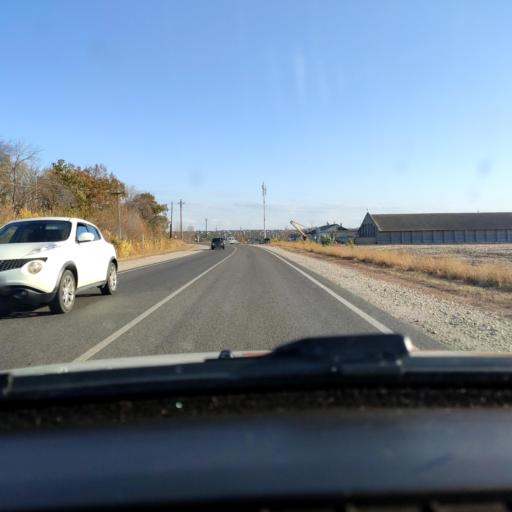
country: RU
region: Voronezj
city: Semiluki
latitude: 51.7244
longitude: 38.9920
